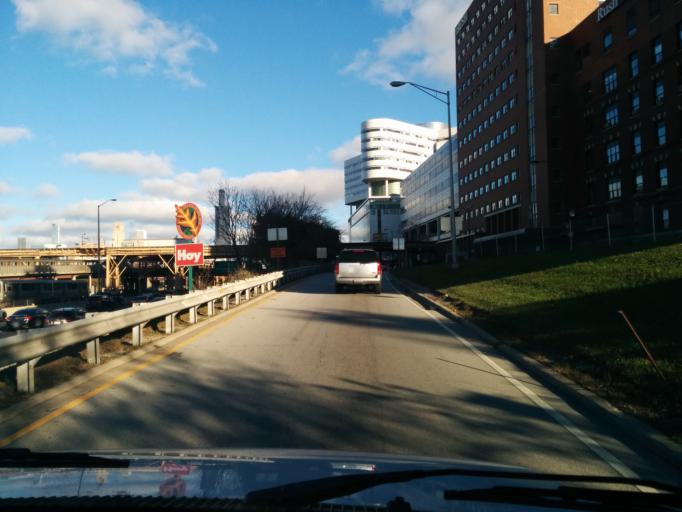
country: US
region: Illinois
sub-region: Cook County
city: Chicago
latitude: 41.8753
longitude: -87.6715
